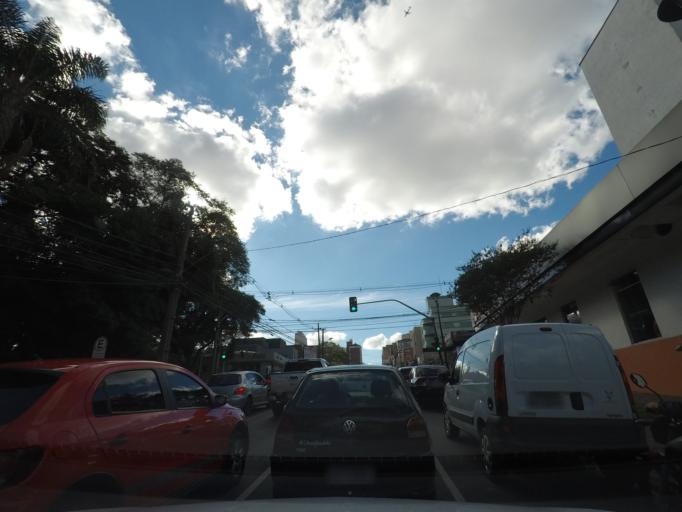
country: BR
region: Parana
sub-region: Curitiba
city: Curitiba
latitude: -25.4462
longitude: -49.2742
